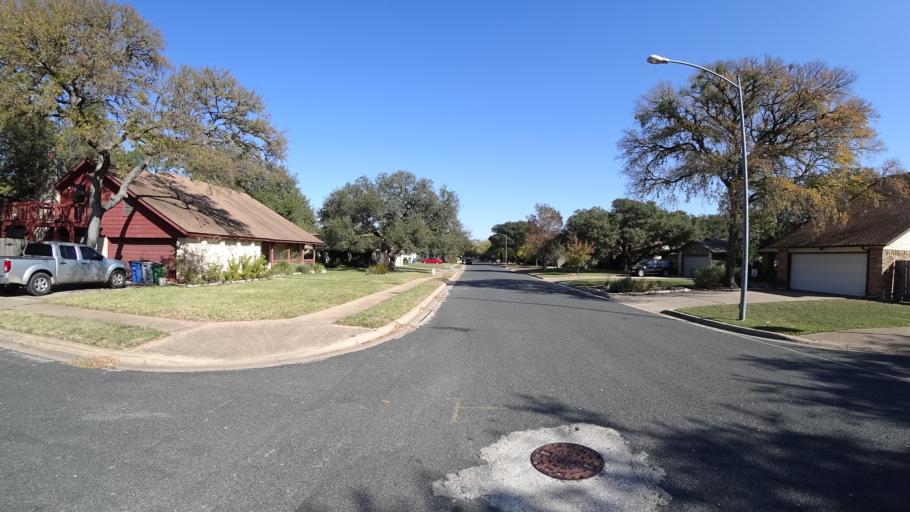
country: US
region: Texas
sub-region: Travis County
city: Shady Hollow
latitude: 30.2223
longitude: -97.8657
